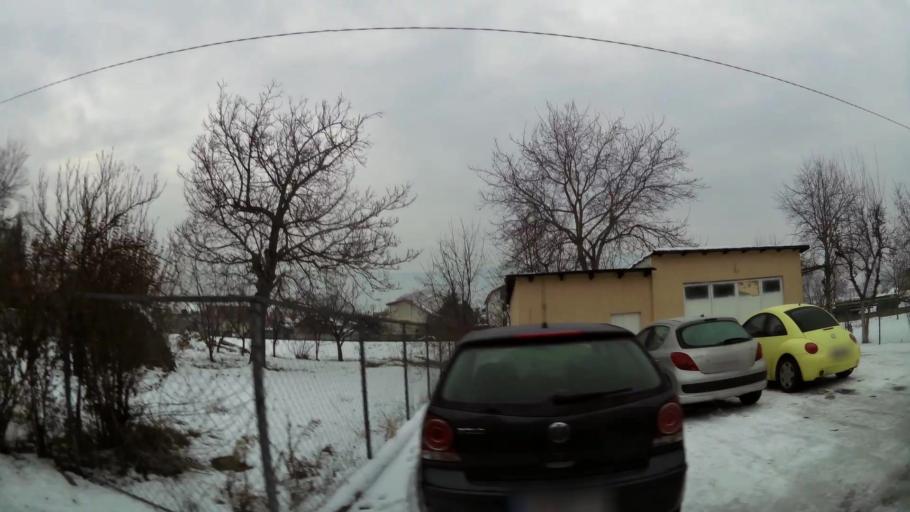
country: MK
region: Saraj
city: Saraj
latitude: 42.0100
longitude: 21.3320
